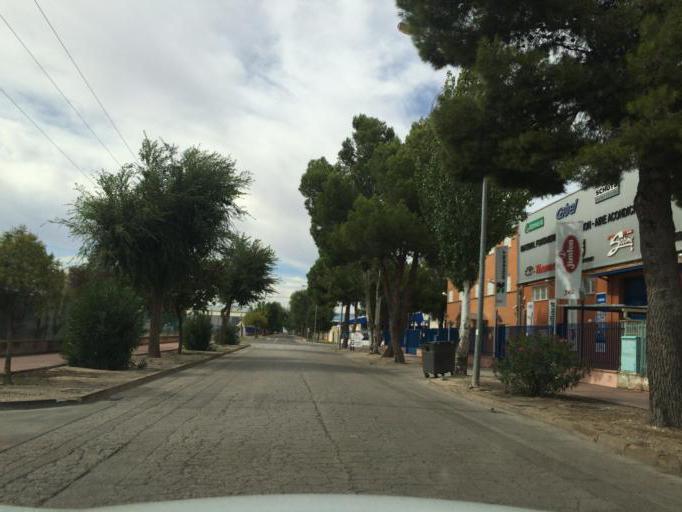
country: ES
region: Castille-La Mancha
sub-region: Provincia de Albacete
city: Albacete
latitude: 39.0161
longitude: -1.8836
